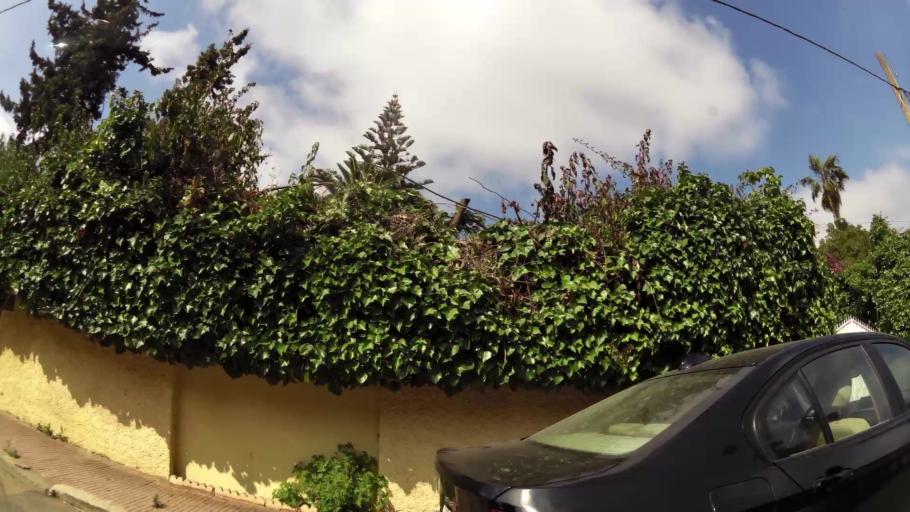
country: MA
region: Rabat-Sale-Zemmour-Zaer
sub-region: Rabat
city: Rabat
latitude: 33.9729
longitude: -6.8461
